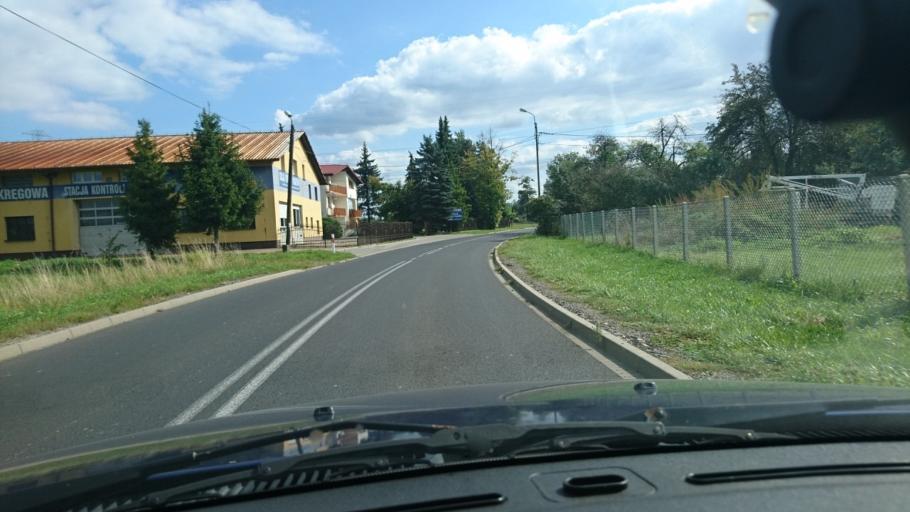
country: PL
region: Silesian Voivodeship
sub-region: Powiat bielski
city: Mazancowice
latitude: 49.8692
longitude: 18.9636
